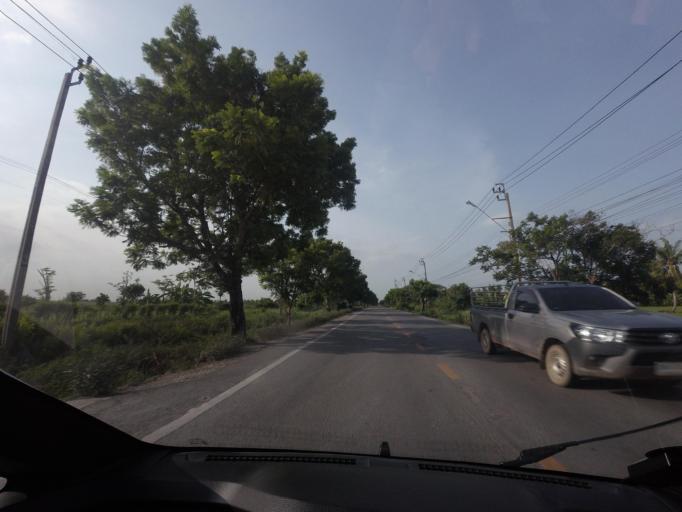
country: TH
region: Bangkok
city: Lat Krabang
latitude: 13.7355
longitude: 100.8620
